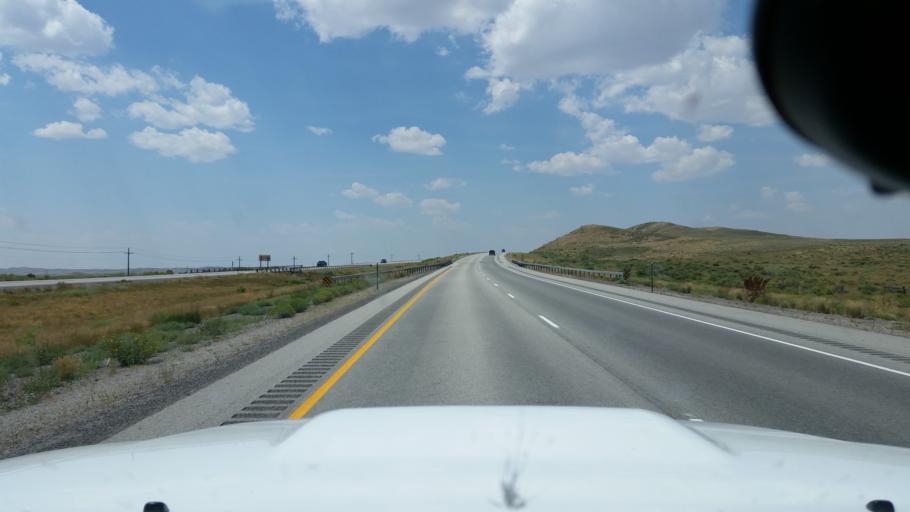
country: US
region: Wyoming
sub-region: Carbon County
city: Rawlins
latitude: 41.7761
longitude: -107.3251
